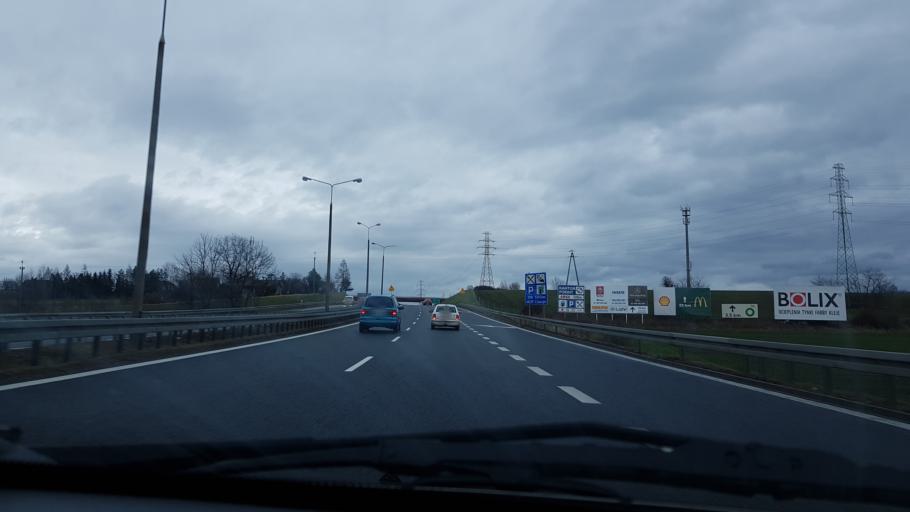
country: PL
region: Silesian Voivodeship
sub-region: Powiat cieszynski
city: Cieszyn
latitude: 49.7661
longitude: 18.6417
